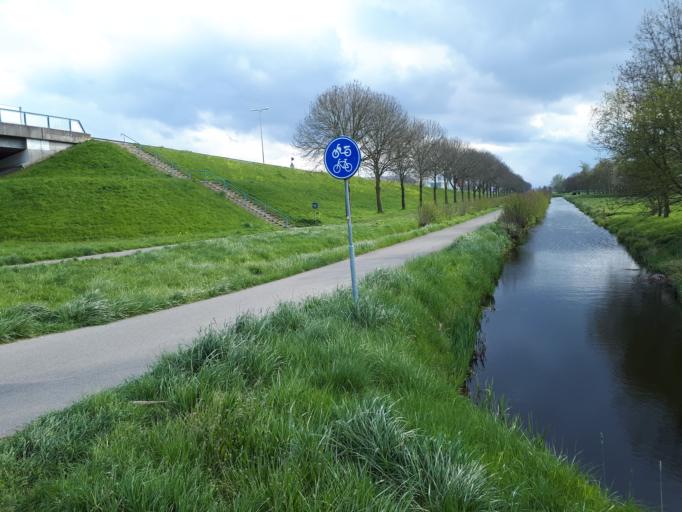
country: NL
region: South Holland
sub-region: Gemeente Alphen aan den Rijn
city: Alphen aan den Rijn
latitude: 52.1171
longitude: 4.6639
